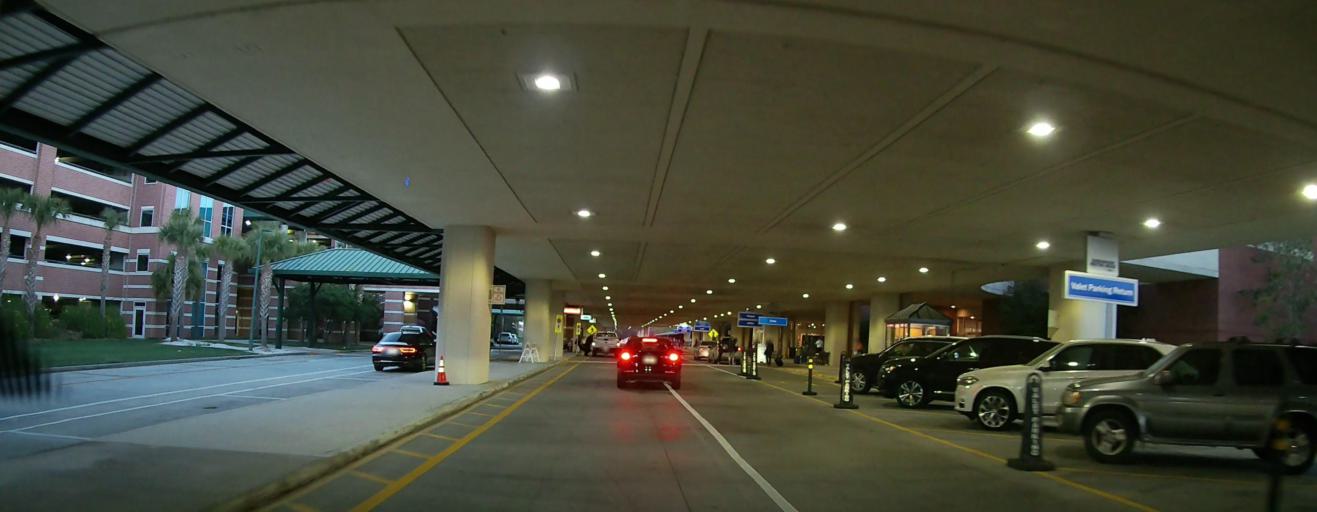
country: US
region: Georgia
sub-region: Chatham County
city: Pooler
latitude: 32.1348
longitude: -81.2104
